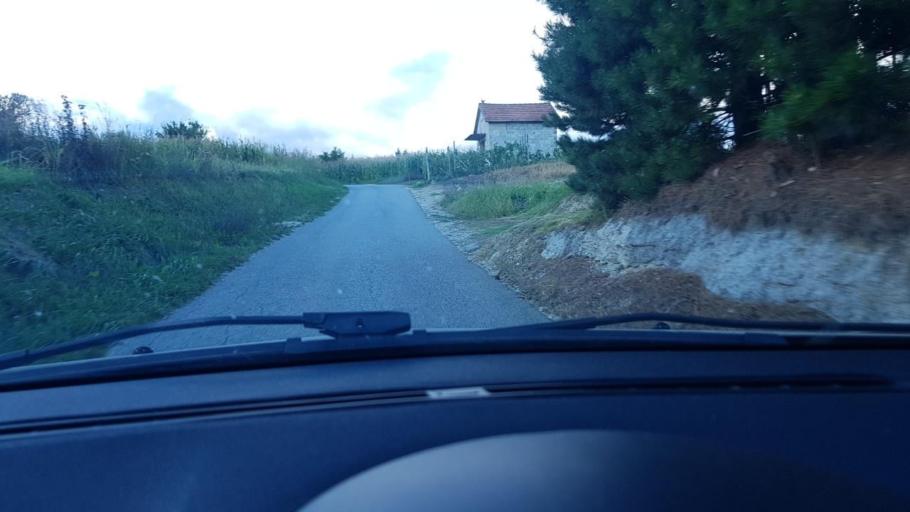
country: HR
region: Krapinsko-Zagorska
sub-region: Grad Krapina
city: Krapina
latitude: 46.1641
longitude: 15.8294
